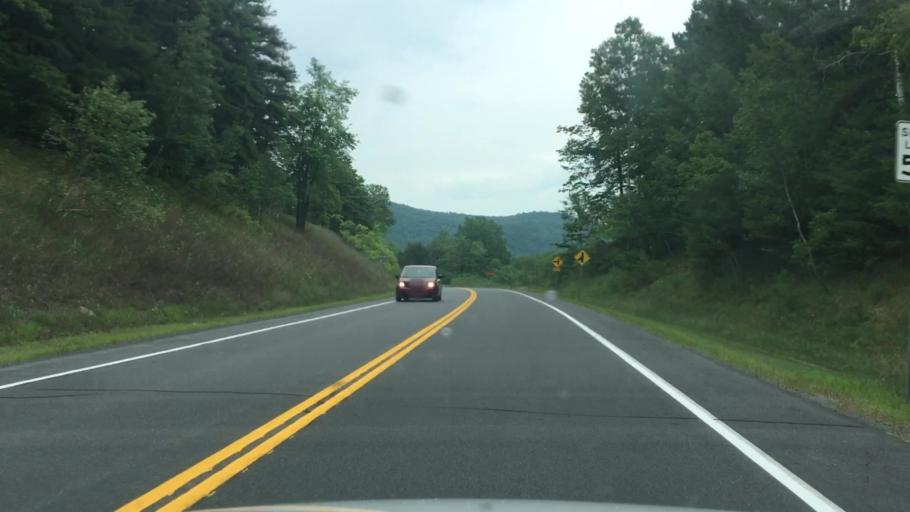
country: US
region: New York
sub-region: Essex County
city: Keeseville
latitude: 44.4650
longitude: -73.5906
